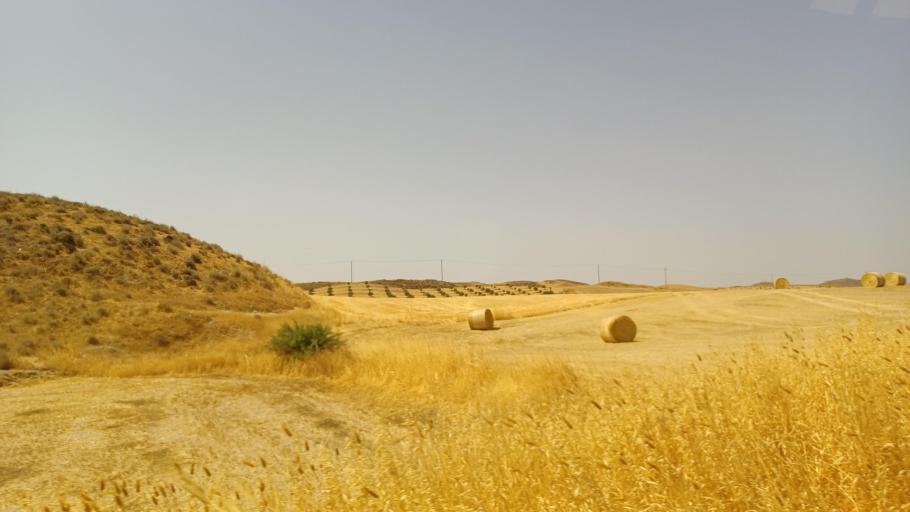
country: CY
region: Larnaka
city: Troulloi
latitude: 35.0310
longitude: 33.5916
